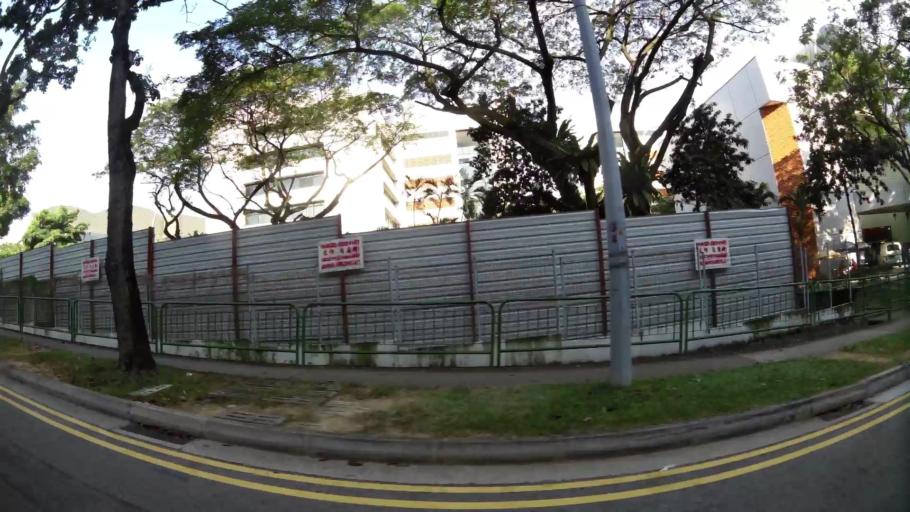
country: SG
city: Singapore
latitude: 1.3256
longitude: 103.8741
